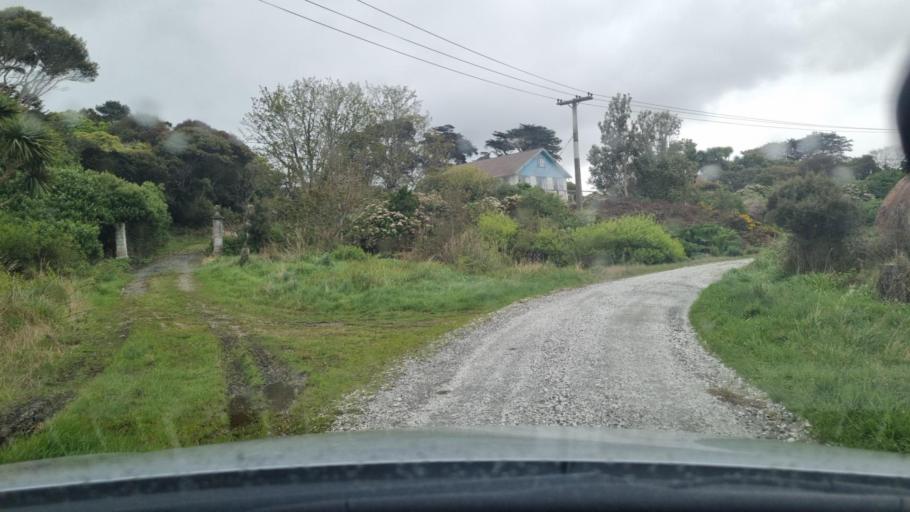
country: NZ
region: Southland
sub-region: Invercargill City
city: Bluff
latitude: -46.5874
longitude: 168.3023
